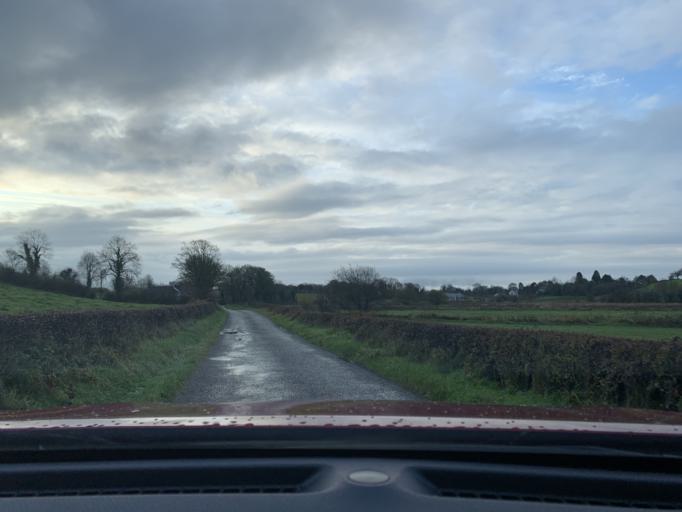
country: IE
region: Connaught
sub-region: Sligo
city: Ballymote
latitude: 54.0430
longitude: -8.5520
